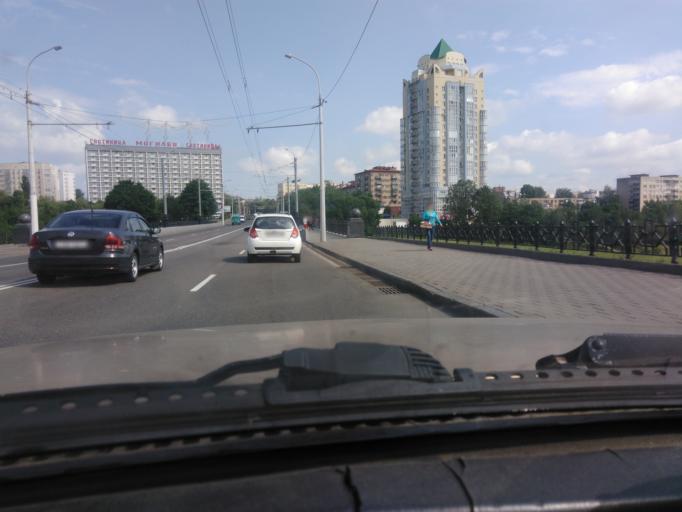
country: BY
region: Mogilev
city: Mahilyow
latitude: 53.9106
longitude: 30.3279
